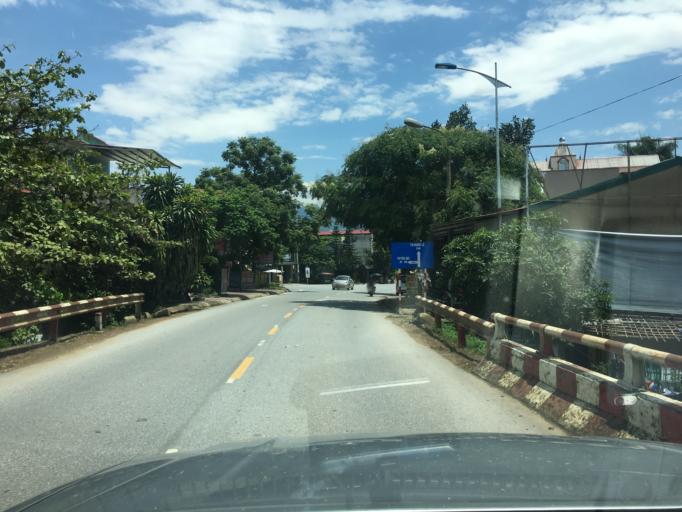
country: VN
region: Yen Bai
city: Son Thinh
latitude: 21.6111
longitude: 104.5062
